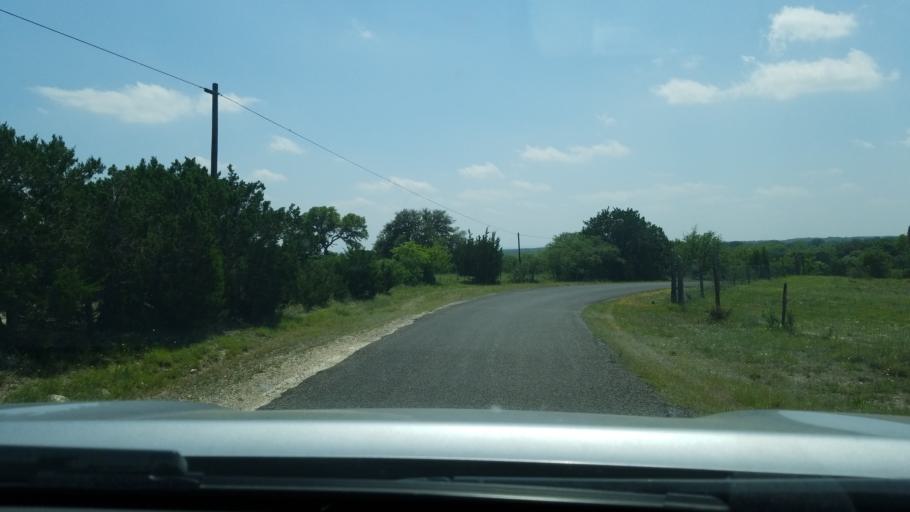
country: US
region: Texas
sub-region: Blanco County
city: Blanco
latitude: 29.9880
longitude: -98.5342
